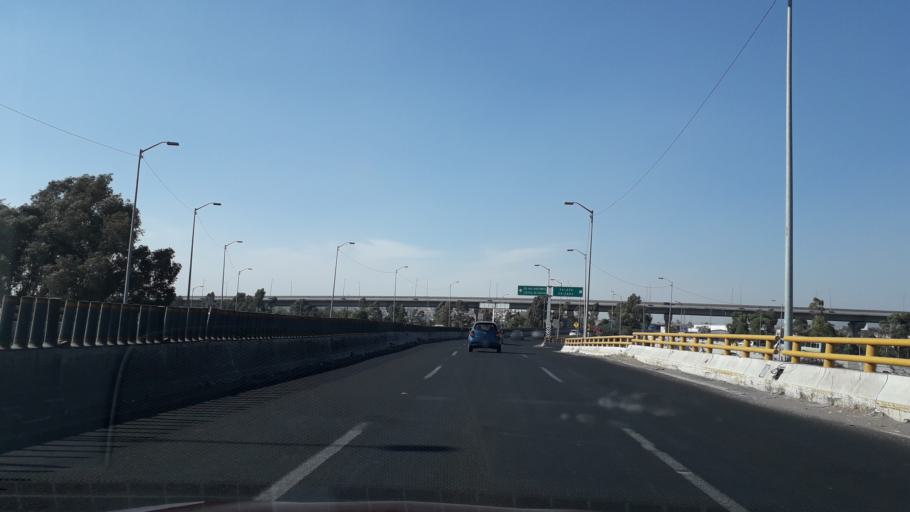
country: MX
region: Puebla
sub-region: Puebla
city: San Sebastian de Aparicio
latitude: 19.0813
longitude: -98.1891
